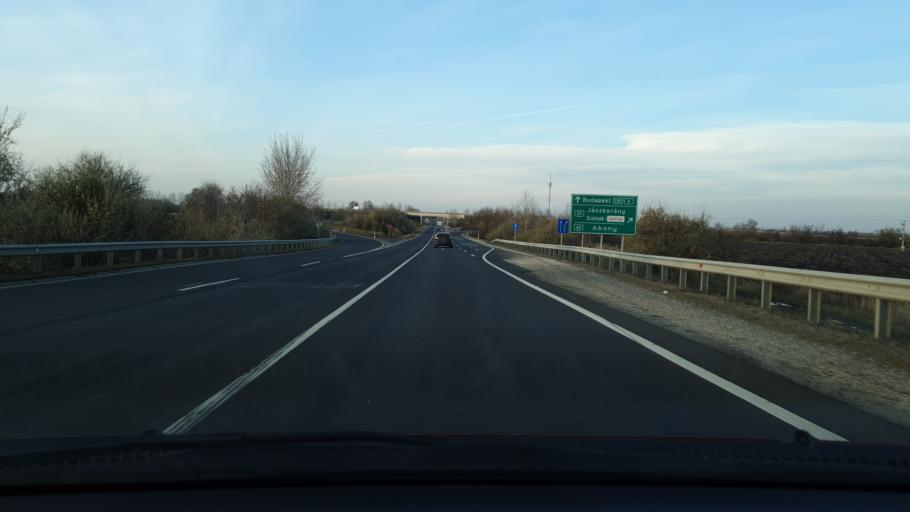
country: HU
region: Jasz-Nagykun-Szolnok
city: Toszeg
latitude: 47.1786
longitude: 20.1005
